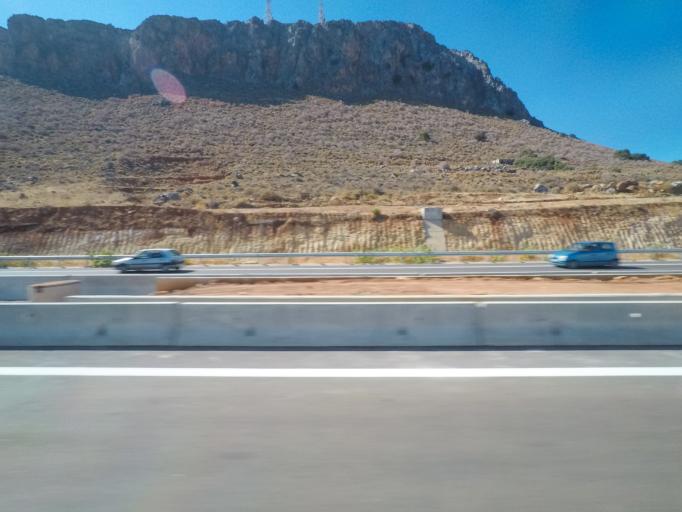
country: GR
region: Crete
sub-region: Nomos Irakleiou
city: Gouvai
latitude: 35.3187
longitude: 25.3209
